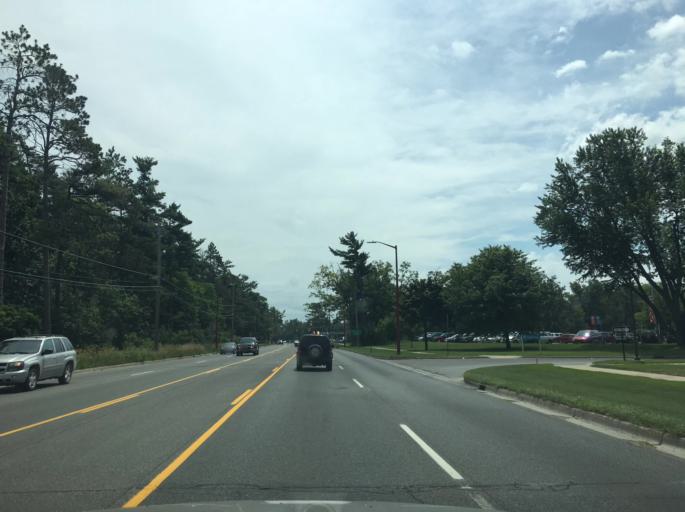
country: US
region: Michigan
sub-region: Grand Traverse County
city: Traverse City
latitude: 44.7578
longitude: -85.5777
